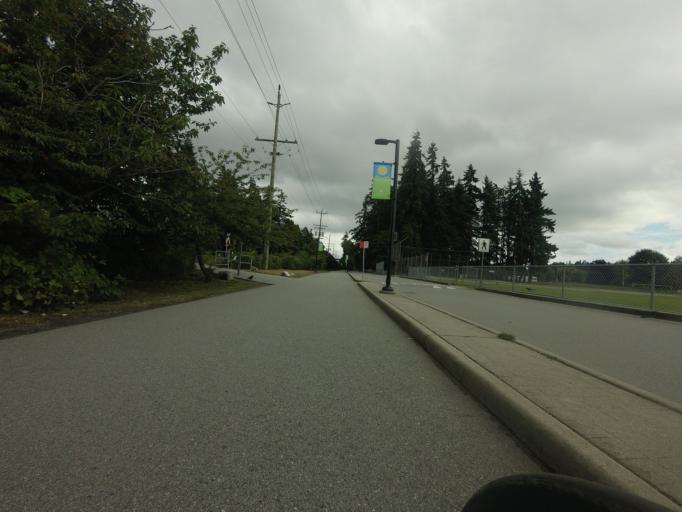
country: CA
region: British Columbia
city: West Vancouver
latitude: 49.3255
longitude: -123.1489
